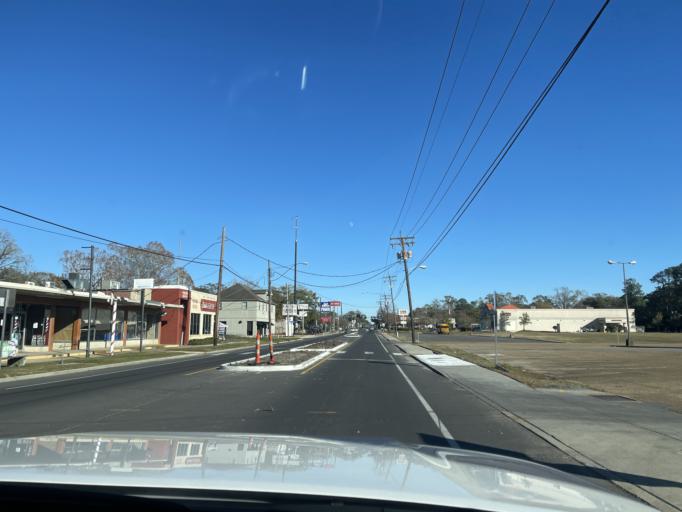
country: US
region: Louisiana
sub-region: East Baton Rouge Parish
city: Baton Rouge
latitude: 30.4441
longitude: -91.1567
